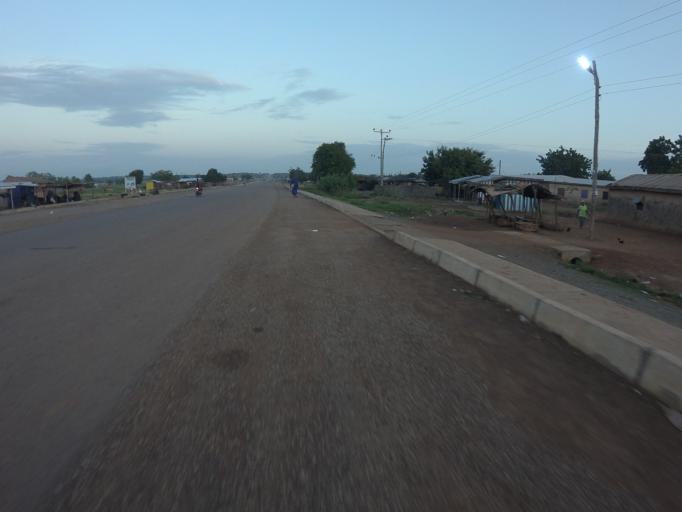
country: GH
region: Northern
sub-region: Yendi
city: Yendi
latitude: 9.9175
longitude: -0.2161
